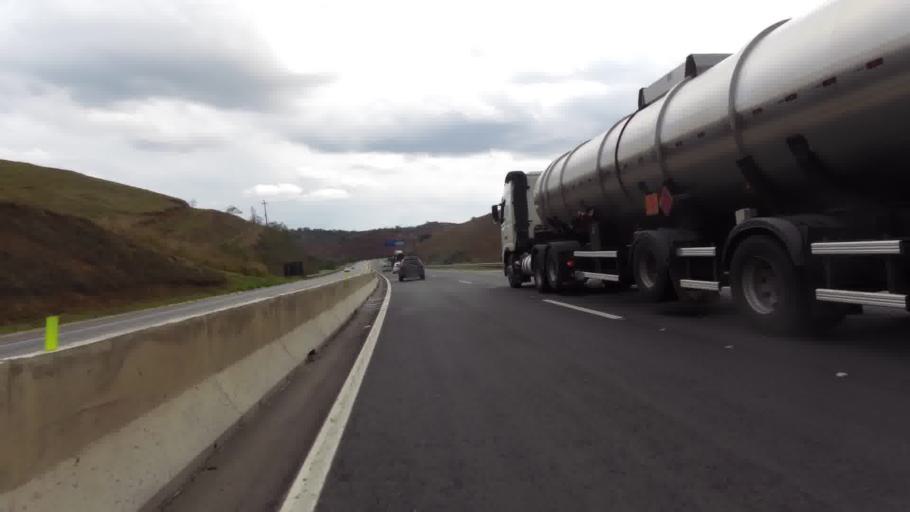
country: BR
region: Rio de Janeiro
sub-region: Casimiro De Abreu
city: Casimiro de Abreu
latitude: -22.4692
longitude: -42.0765
